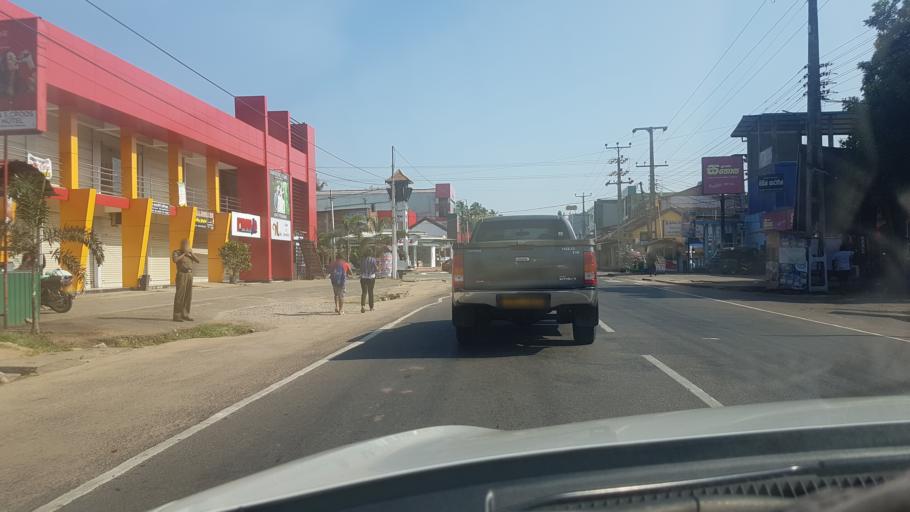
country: LK
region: North Western
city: Chilaw
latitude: 7.4136
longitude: 79.8310
